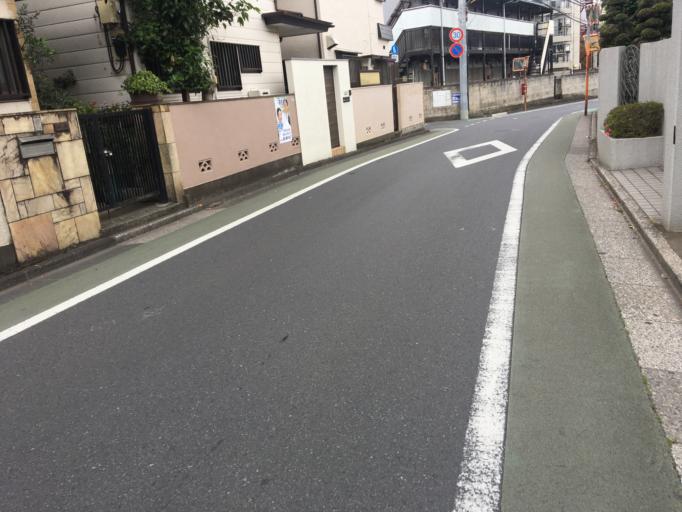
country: JP
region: Tokyo
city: Kokubunji
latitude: 35.6972
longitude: 139.4890
